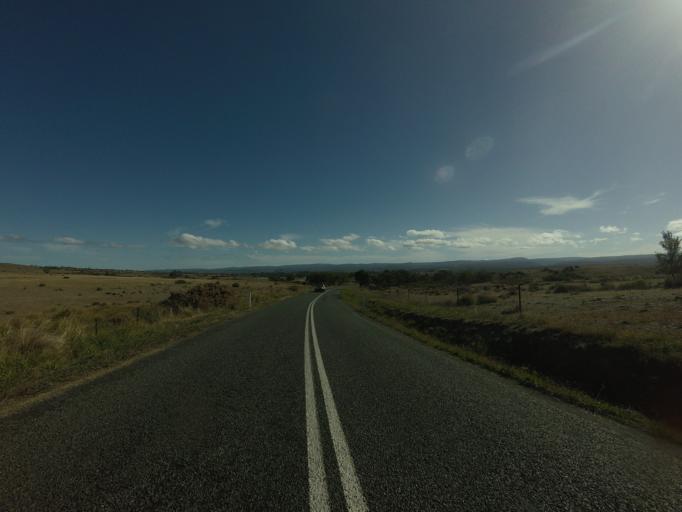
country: AU
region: Tasmania
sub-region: Break O'Day
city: St Helens
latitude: -41.9968
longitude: 148.0922
